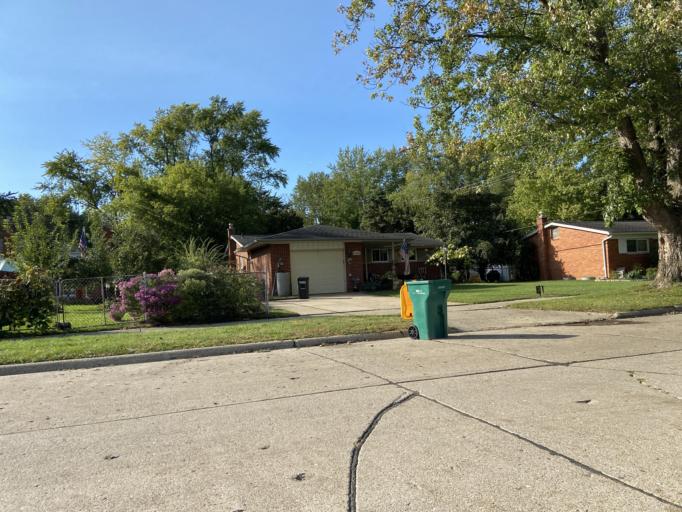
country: US
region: Michigan
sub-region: Oakland County
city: Farmington
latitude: 42.4515
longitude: -83.3231
